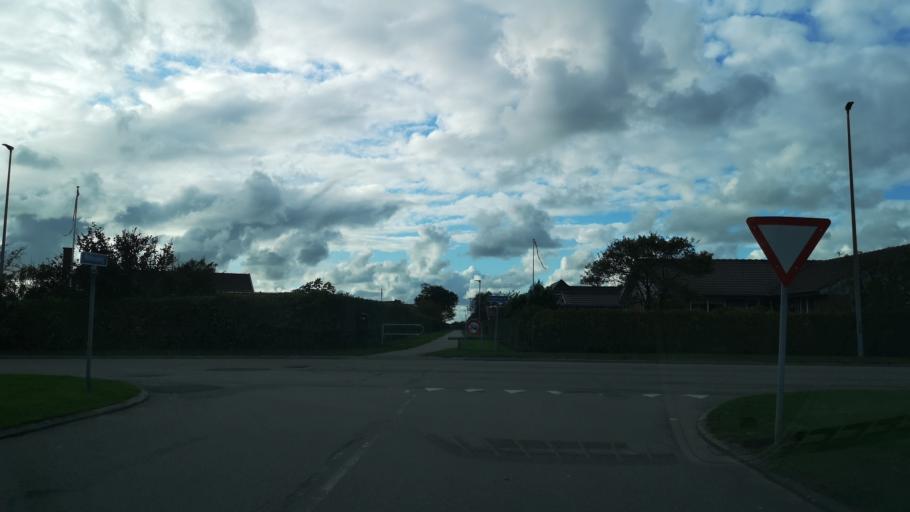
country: DK
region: Central Jutland
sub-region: Ringkobing-Skjern Kommune
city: Ringkobing
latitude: 56.0886
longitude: 8.2665
